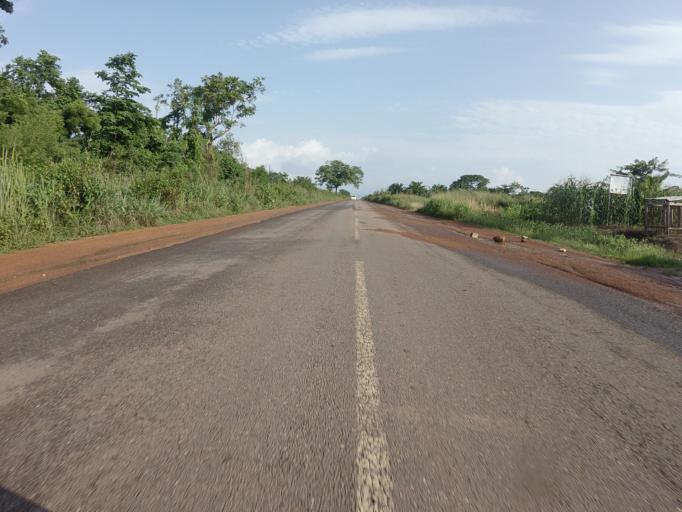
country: GH
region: Volta
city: Hohoe
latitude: 7.0299
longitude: 0.4275
